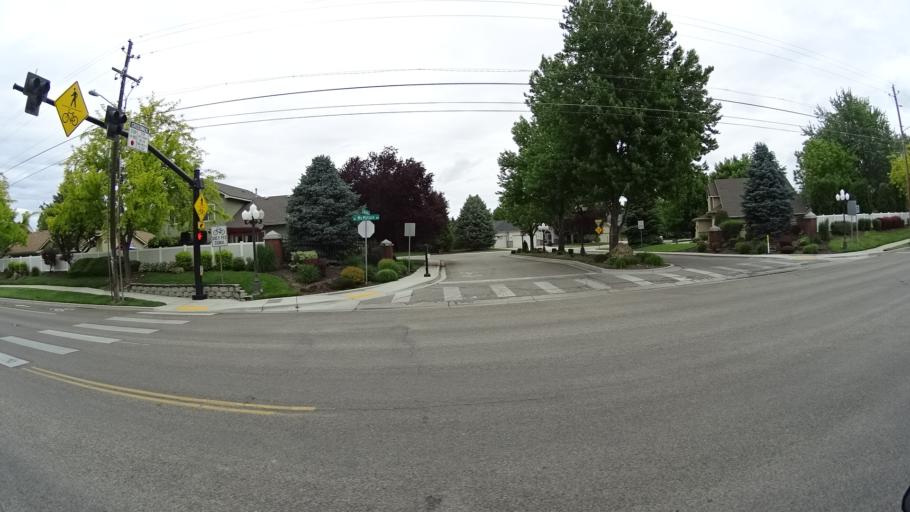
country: US
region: Idaho
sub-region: Ada County
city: Eagle
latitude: 43.6485
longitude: -116.3245
